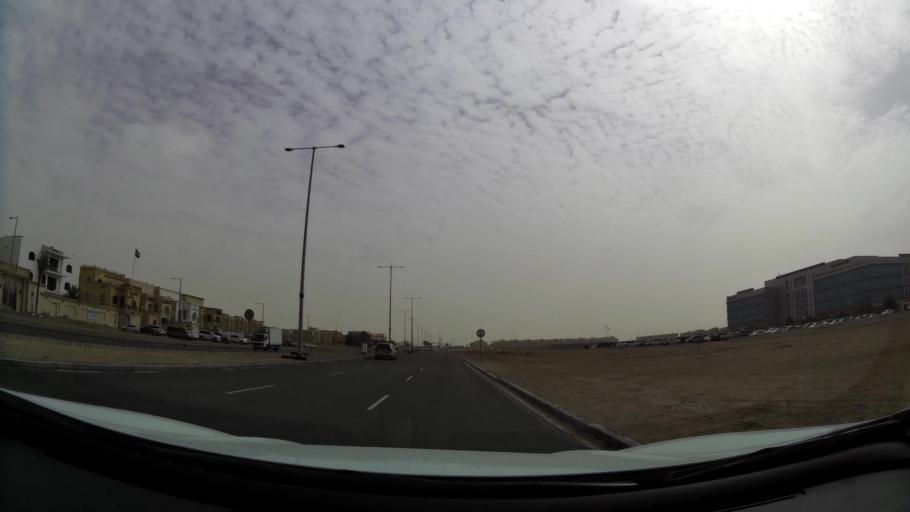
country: AE
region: Abu Dhabi
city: Abu Dhabi
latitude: 24.4081
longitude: 54.5706
